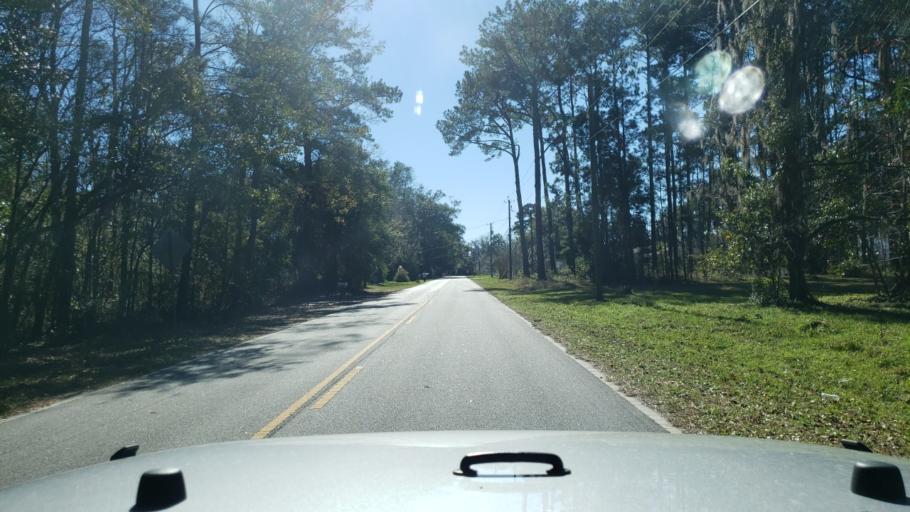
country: US
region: Georgia
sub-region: Chatham County
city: Georgetown
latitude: 32.0371
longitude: -81.1876
